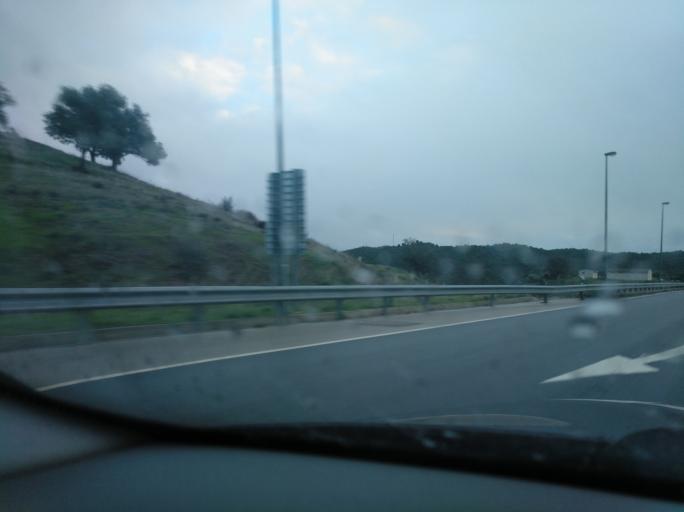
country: PT
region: Faro
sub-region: Castro Marim
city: Castro Marim
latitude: 37.3316
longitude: -7.4881
